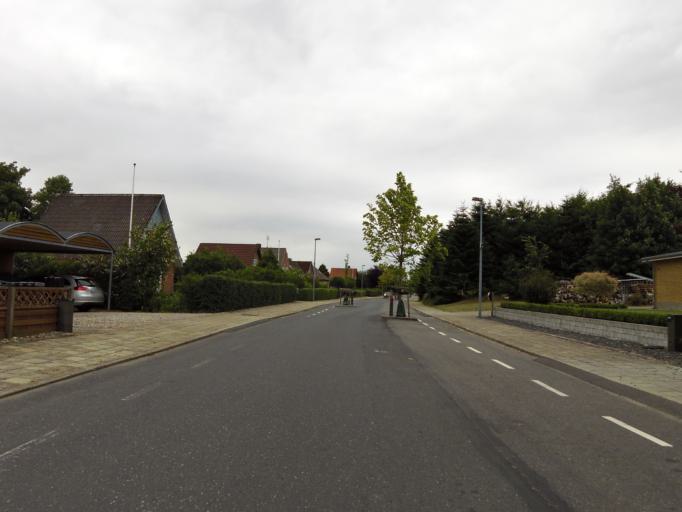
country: DK
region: South Denmark
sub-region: Tonder Kommune
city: Logumkloster
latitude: 55.0712
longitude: 8.9332
